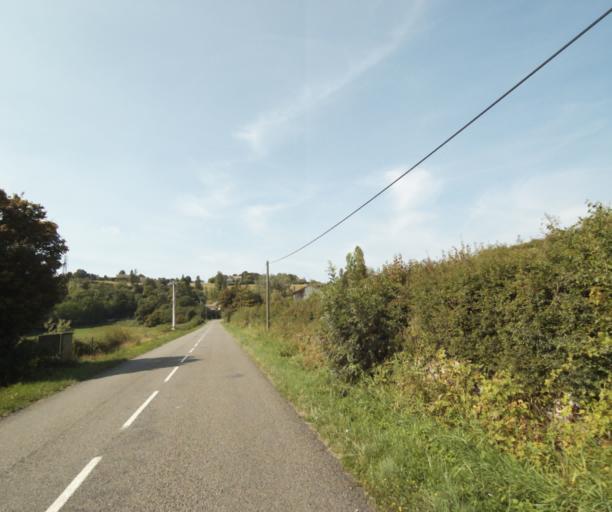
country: FR
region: Bourgogne
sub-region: Departement de Saone-et-Loire
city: Tournus
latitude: 46.5641
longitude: 4.8845
